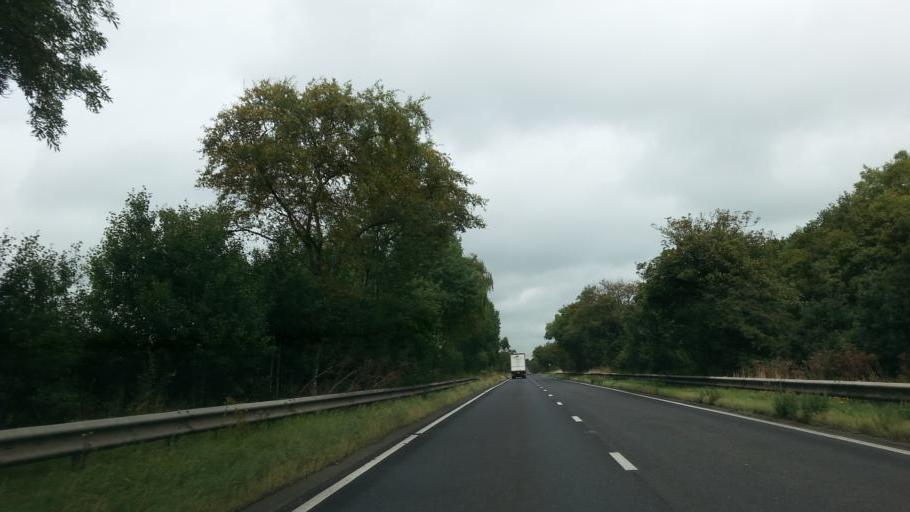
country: GB
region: England
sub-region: Leicestershire
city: Queniborough
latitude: 52.7715
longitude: -1.0513
